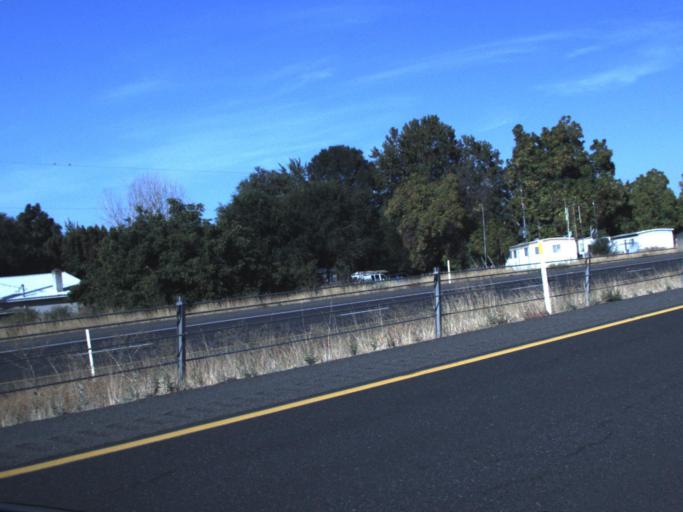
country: US
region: Washington
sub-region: Yakima County
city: Gleed
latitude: 46.6574
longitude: -120.6184
